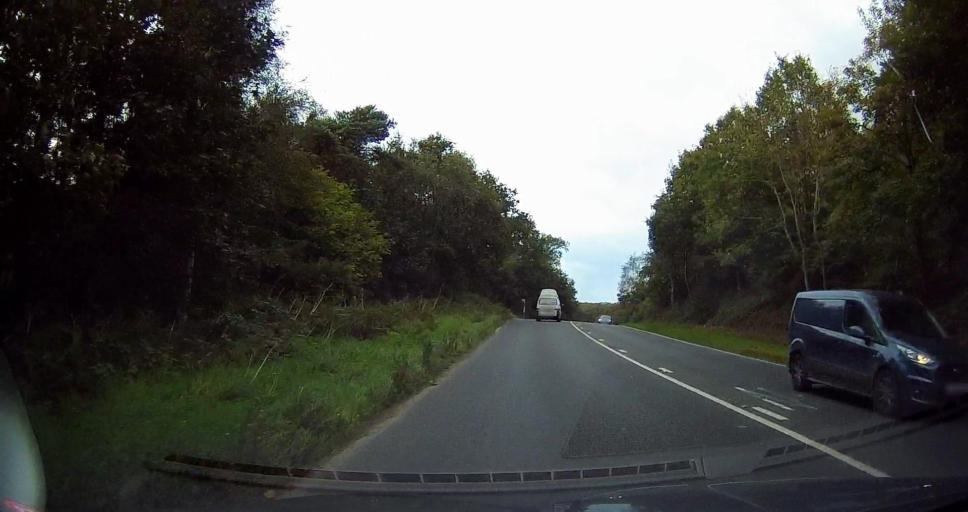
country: GB
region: England
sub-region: Kent
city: Harrietsham
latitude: 51.2504
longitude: 0.6363
